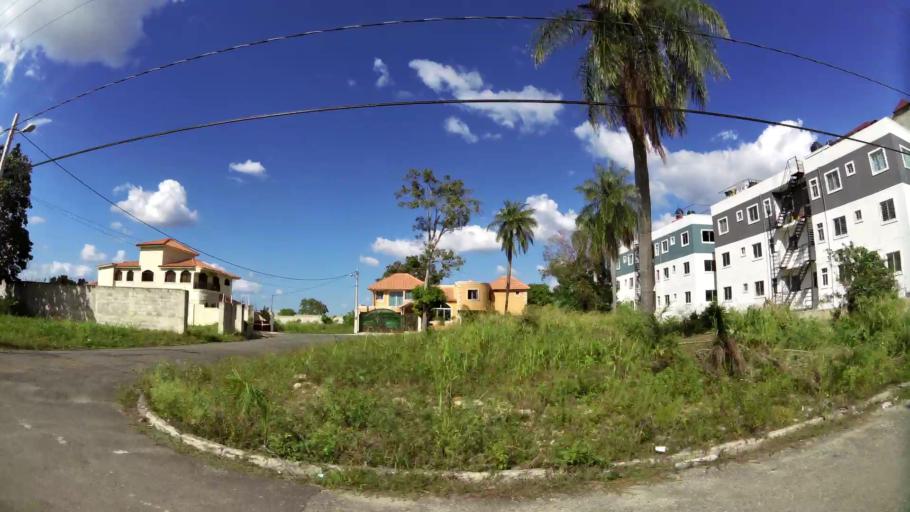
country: DO
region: Santo Domingo
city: Santo Domingo Oeste
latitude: 18.5077
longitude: -70.0000
